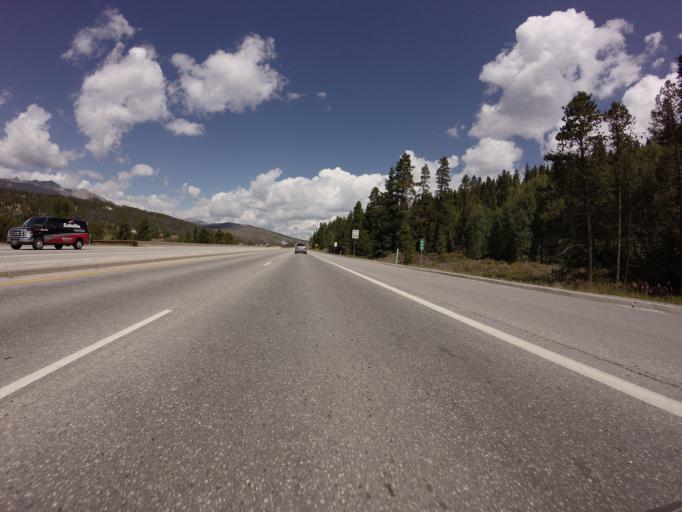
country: US
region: Colorado
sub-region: Summit County
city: Breckenridge
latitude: 39.4985
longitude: -106.0463
